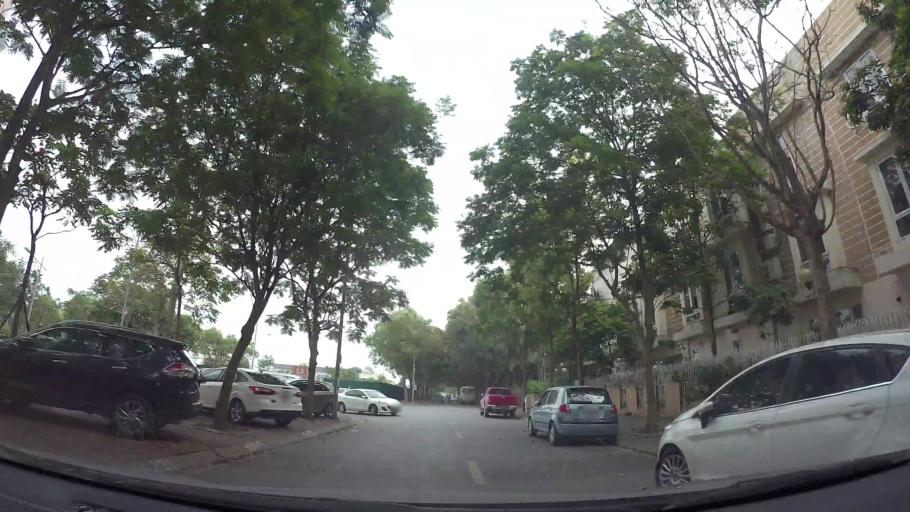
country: VN
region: Ha Noi
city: Trau Quy
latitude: 21.0573
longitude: 105.9059
